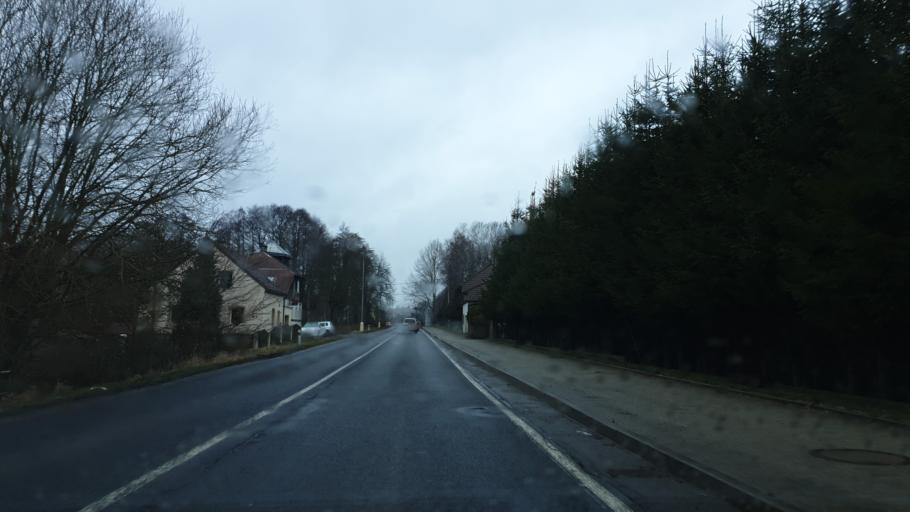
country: CZ
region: Karlovarsky
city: As
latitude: 50.2010
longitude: 12.2112
